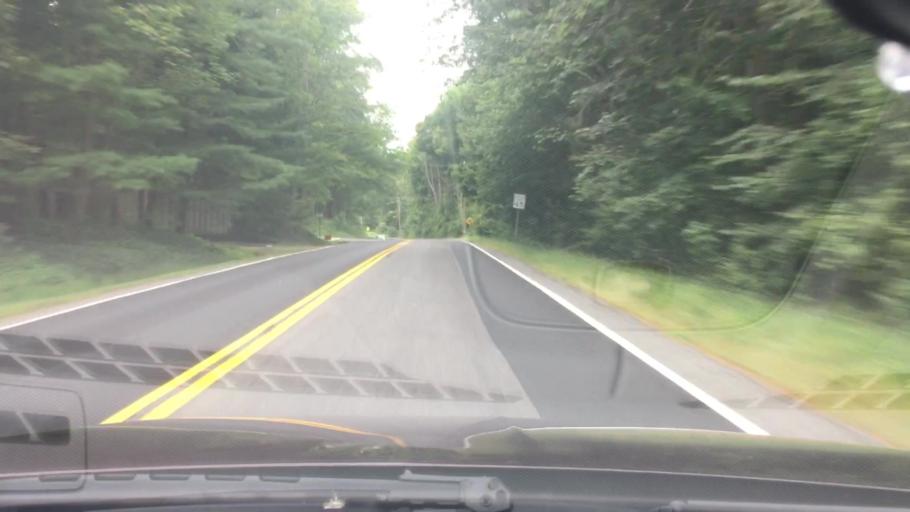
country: US
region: New York
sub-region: Dutchess County
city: Millbrook
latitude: 41.7932
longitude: -73.6904
